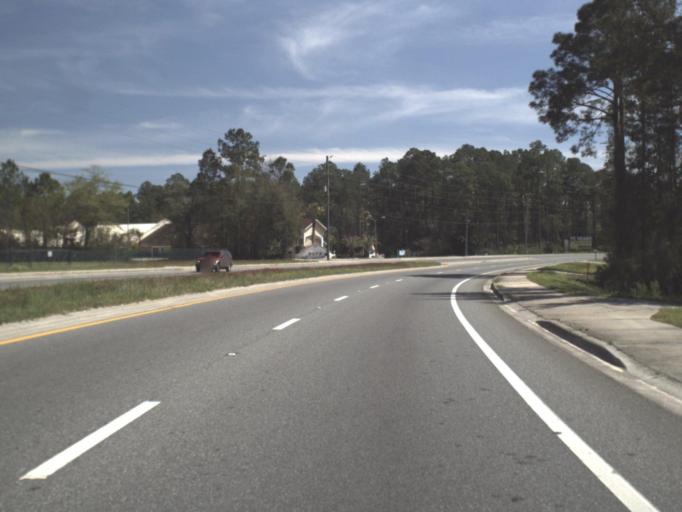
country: US
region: Florida
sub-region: Bay County
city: Lynn Haven
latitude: 30.2838
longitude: -85.6355
